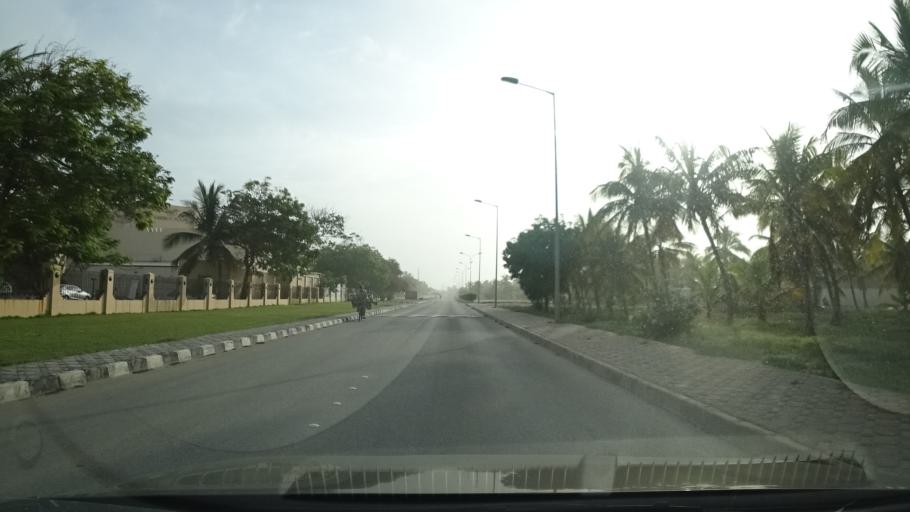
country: OM
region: Zufar
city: Salalah
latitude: 17.0096
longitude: 54.1525
